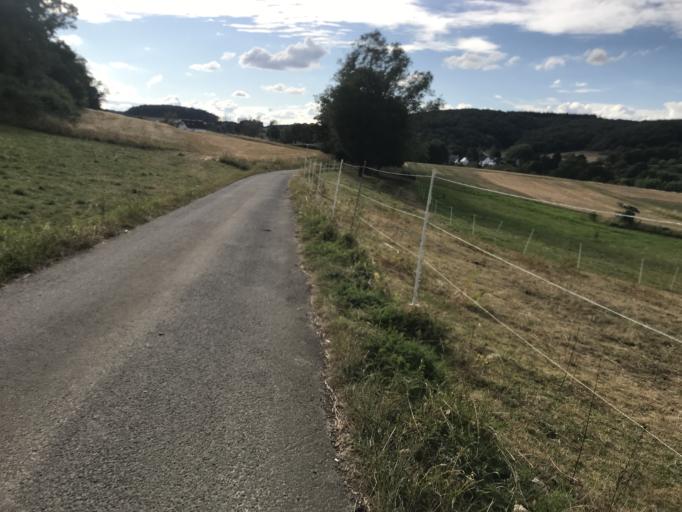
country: DE
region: Hesse
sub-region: Regierungsbezirk Giessen
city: Lohra
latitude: 50.6723
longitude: 8.5819
